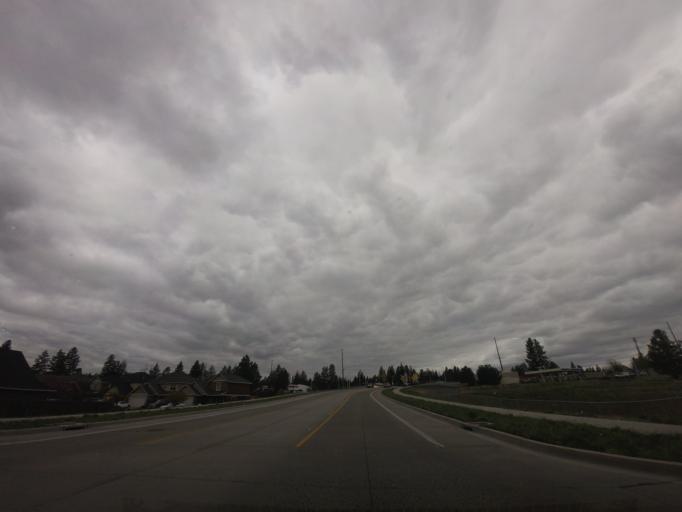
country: US
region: Oregon
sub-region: Deschutes County
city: Bend
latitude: 44.0191
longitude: -121.3149
